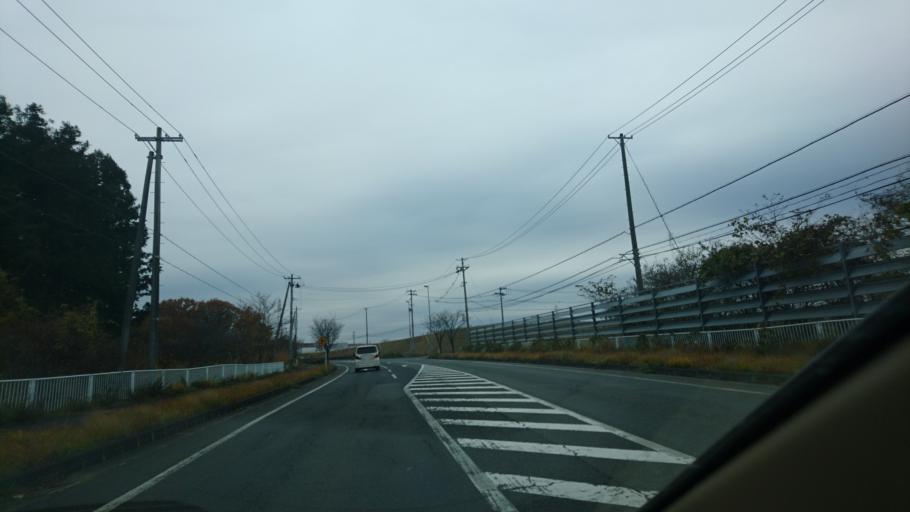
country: JP
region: Iwate
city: Kitakami
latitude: 39.2373
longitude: 141.0928
